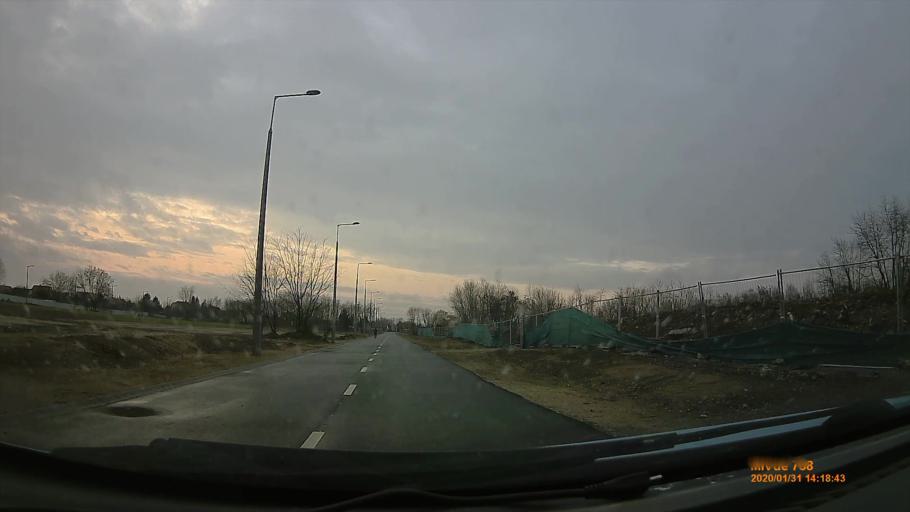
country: HU
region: Szabolcs-Szatmar-Bereg
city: Nyiregyhaza
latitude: 47.9534
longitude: 21.6804
